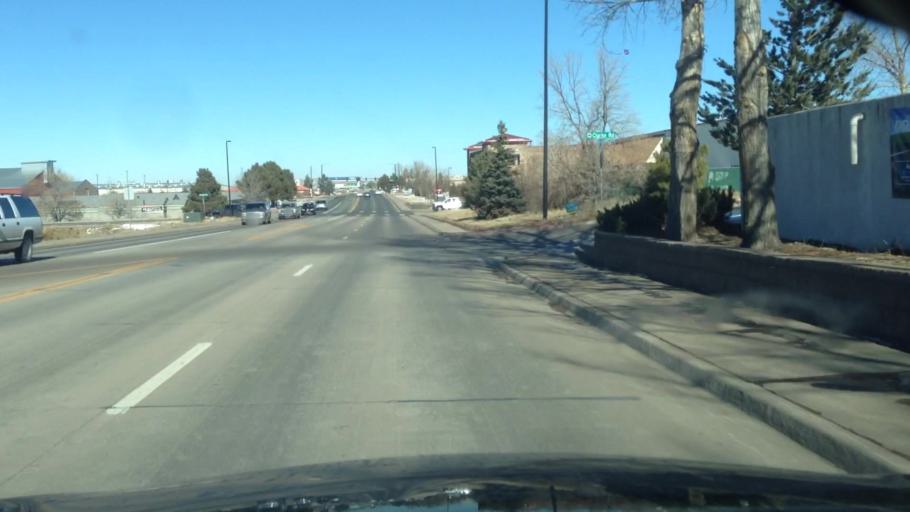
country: US
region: Colorado
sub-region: Douglas County
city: Parker
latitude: 39.5231
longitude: -104.7710
